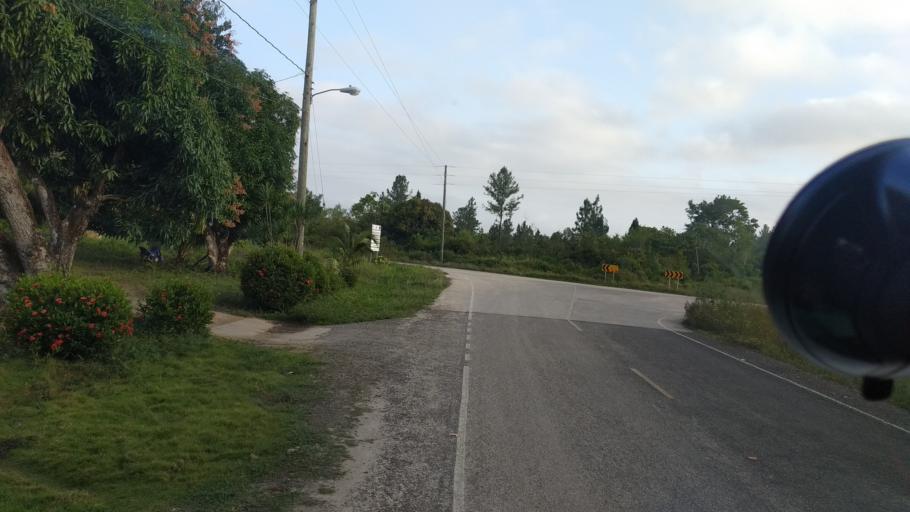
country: BZ
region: Stann Creek
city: Placencia
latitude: 16.5744
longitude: -88.5298
